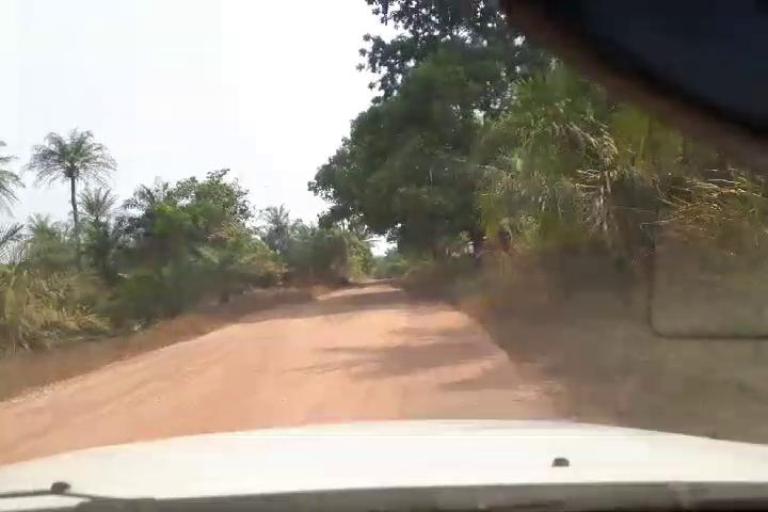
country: SL
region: Northern Province
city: Masingbi
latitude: 8.7904
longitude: -11.8700
